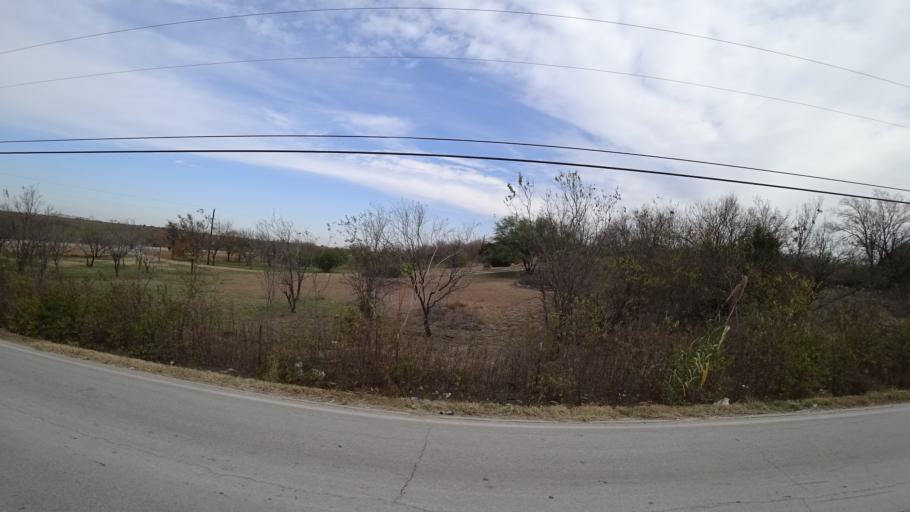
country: US
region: Texas
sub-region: Travis County
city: Onion Creek
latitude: 30.1293
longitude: -97.6837
